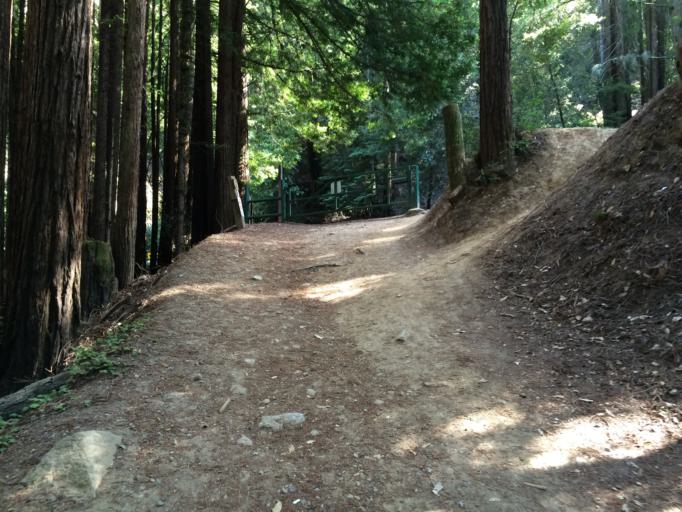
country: US
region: California
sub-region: Santa Cruz County
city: Mount Hermon
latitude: 37.0311
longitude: -122.0631
